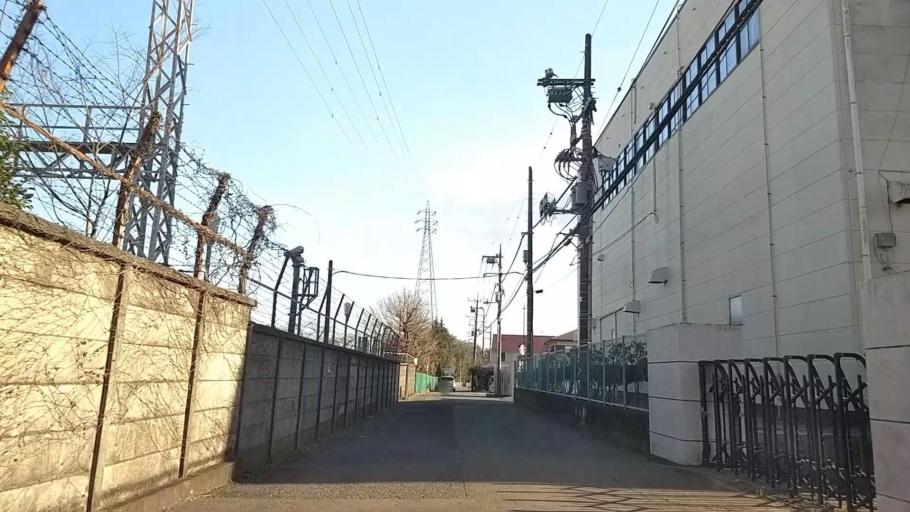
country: JP
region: Kanagawa
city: Atsugi
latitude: 35.4582
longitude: 139.3270
